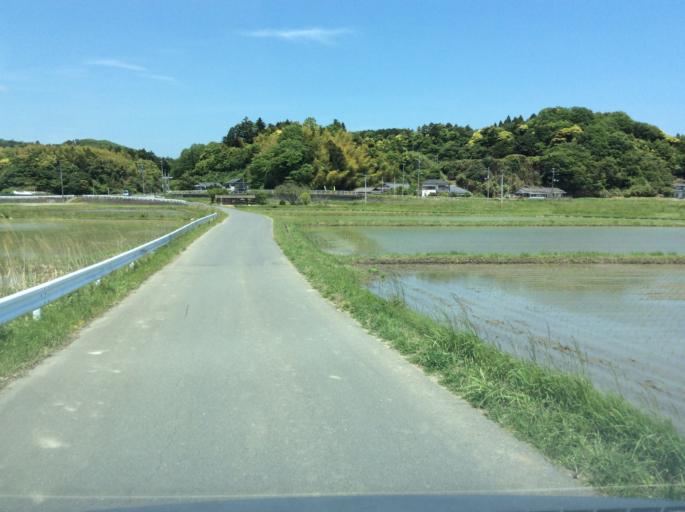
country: JP
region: Fukushima
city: Iwaki
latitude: 37.0286
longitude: 140.9430
